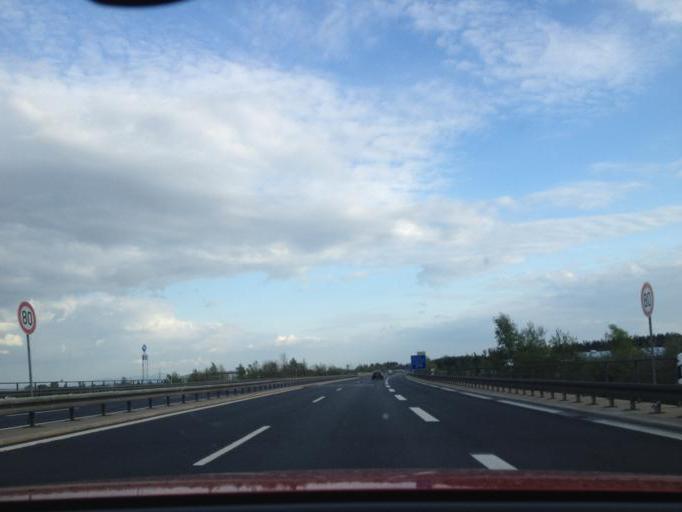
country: DE
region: Bavaria
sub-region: Upper Palatinate
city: Mitterteich
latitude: 49.9403
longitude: 12.2237
